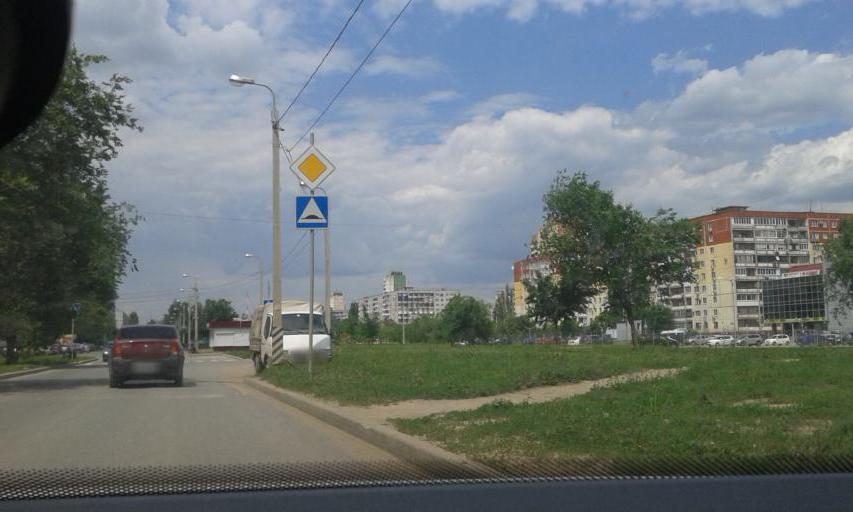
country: RU
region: Volgograd
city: Volgograd
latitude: 48.7506
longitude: 44.5049
